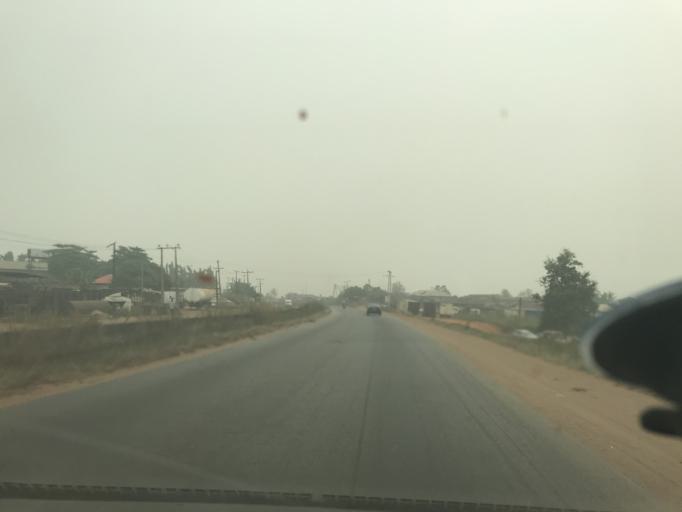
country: NG
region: Ogun
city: Shagamu
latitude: 6.8600
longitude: 3.6237
